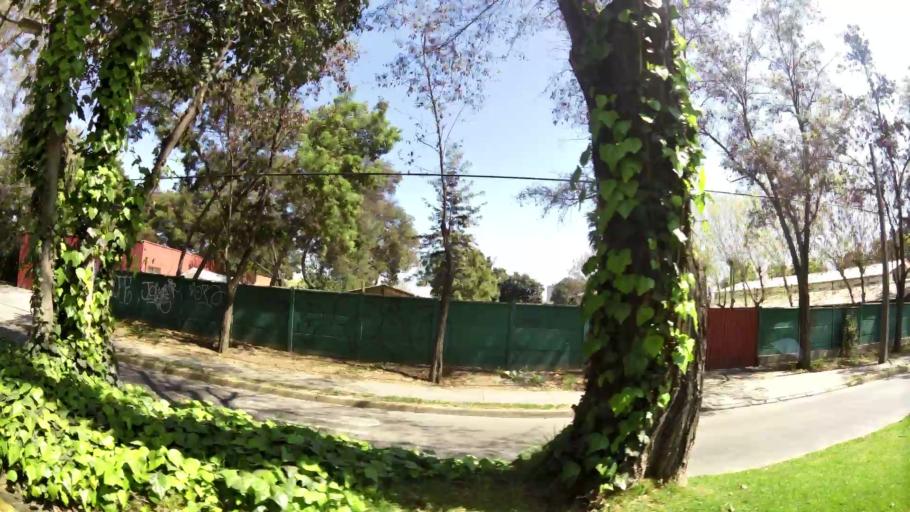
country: CL
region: Santiago Metropolitan
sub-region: Provincia de Santiago
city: Villa Presidente Frei, Nunoa, Santiago, Chile
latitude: -33.4201
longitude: -70.5463
